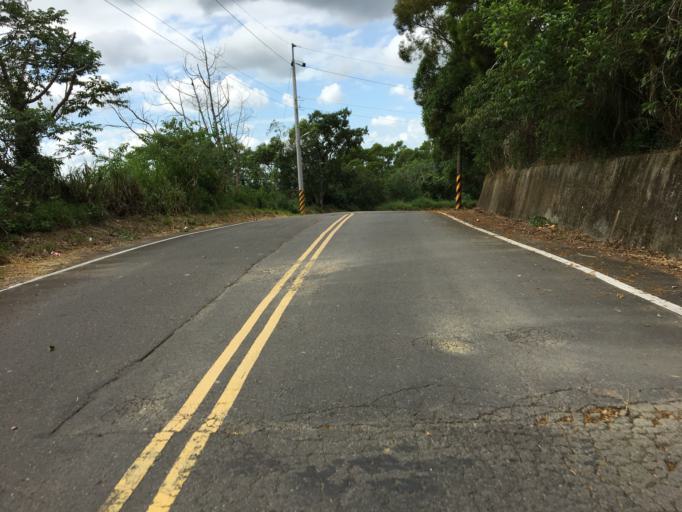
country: TW
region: Taiwan
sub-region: Hsinchu
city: Hsinchu
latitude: 24.7099
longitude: 120.9539
